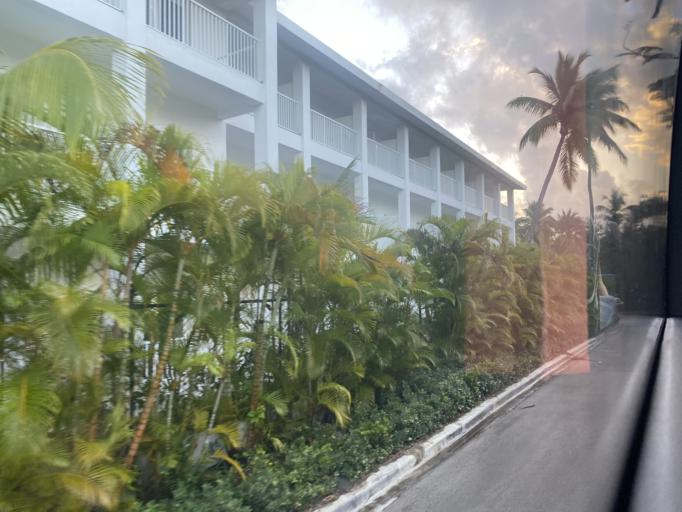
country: DO
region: San Juan
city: Punta Cana
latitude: 18.7196
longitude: -68.4571
